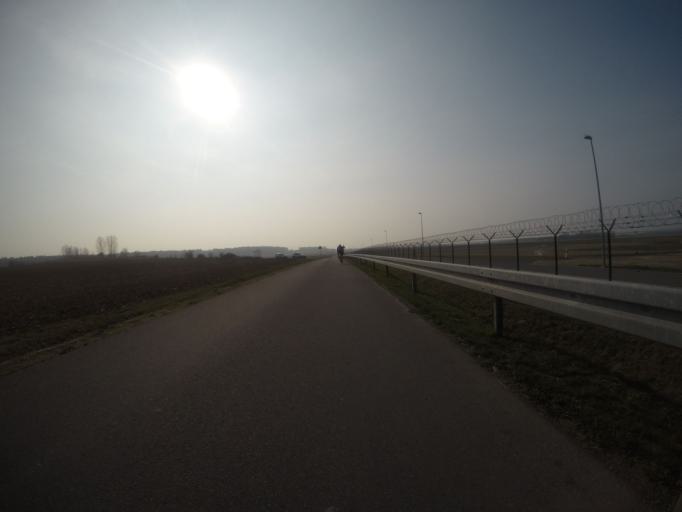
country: DE
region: Brandenburg
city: Schonefeld
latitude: 52.3460
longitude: 13.4834
